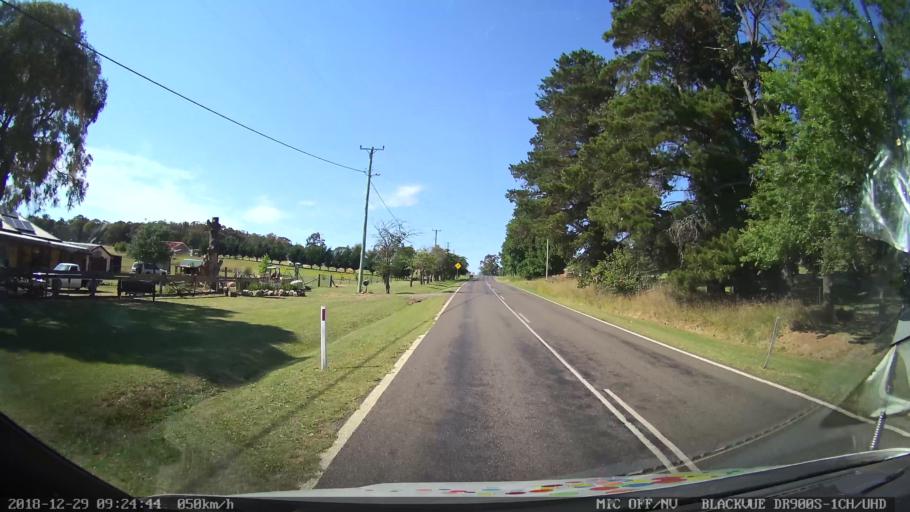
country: AU
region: New South Wales
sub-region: Upper Lachlan Shire
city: Crookwell
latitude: -34.5389
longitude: 149.3938
